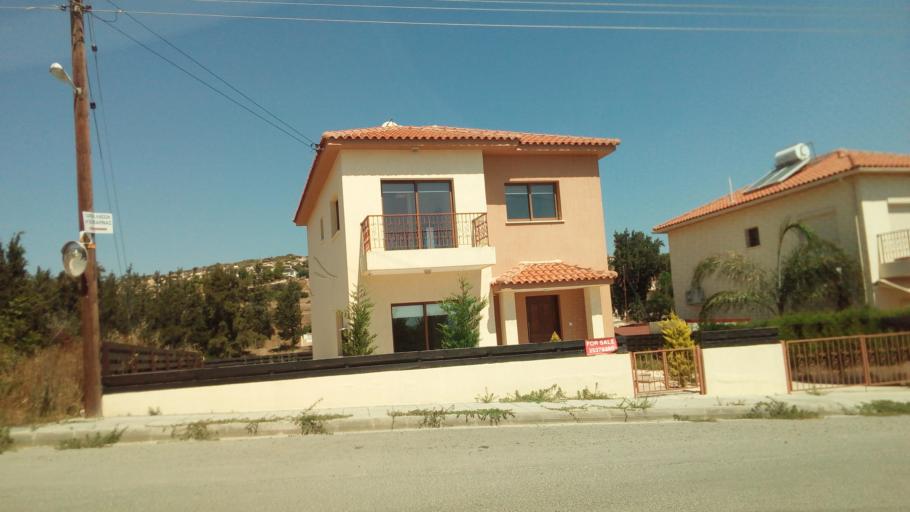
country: CY
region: Limassol
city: Pyrgos
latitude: 34.7331
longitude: 33.1763
